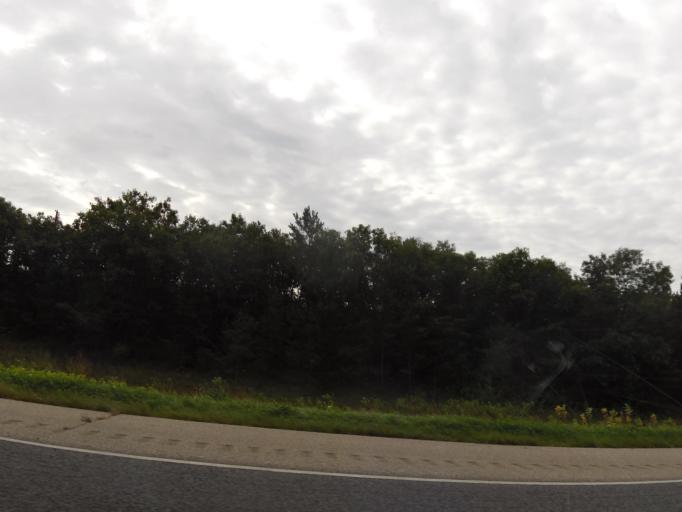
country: US
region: Wisconsin
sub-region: Monroe County
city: Tomah
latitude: 43.9394
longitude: -90.6283
